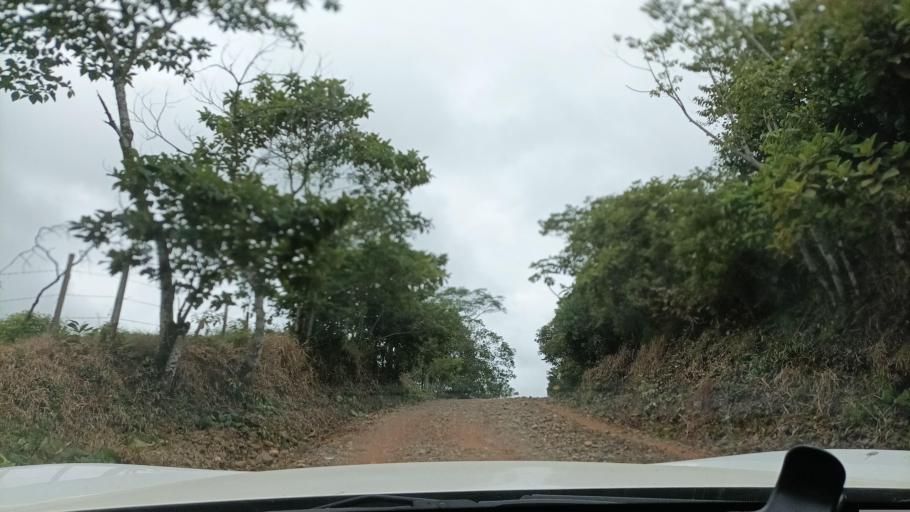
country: MX
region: Veracruz
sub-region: Uxpanapa
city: Poblado 10
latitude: 17.4426
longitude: -94.4045
